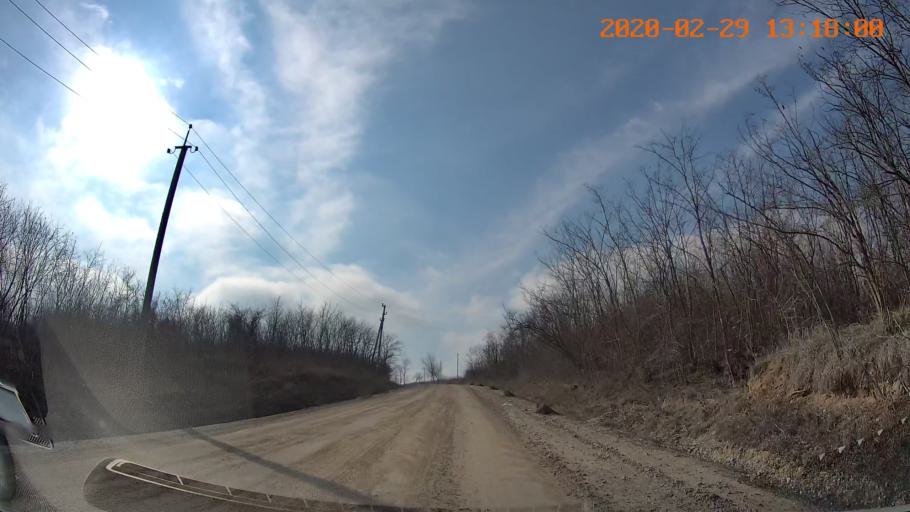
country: MD
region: Telenesti
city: Camenca
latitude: 47.9949
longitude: 28.6602
